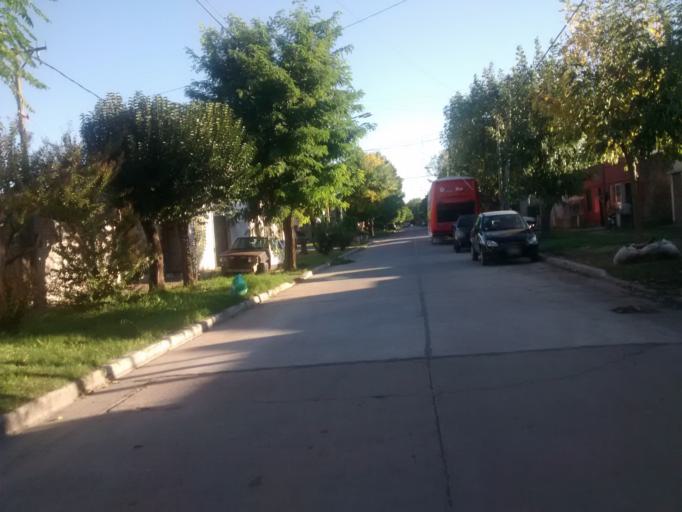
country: AR
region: Buenos Aires
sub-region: Partido de La Plata
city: La Plata
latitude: -34.8961
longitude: -57.9320
